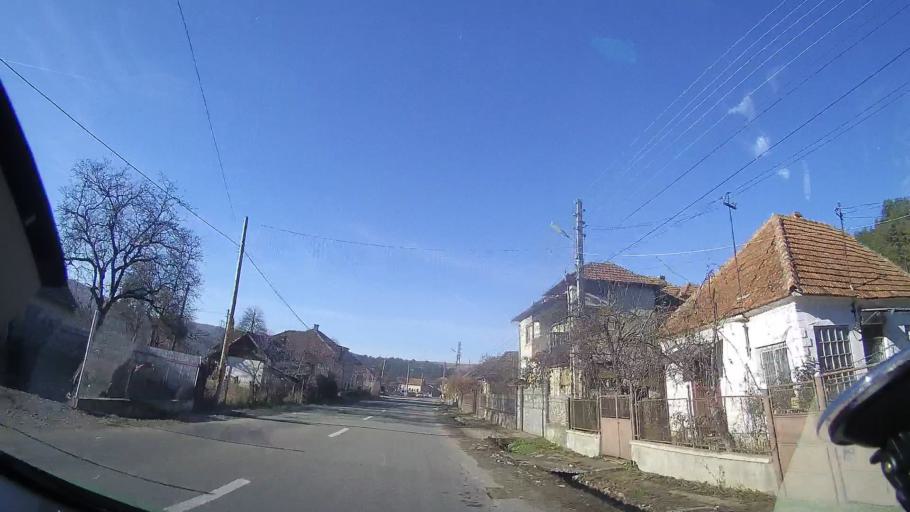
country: RO
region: Bihor
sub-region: Comuna Bratca
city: Bratca
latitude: 46.9289
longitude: 22.6046
